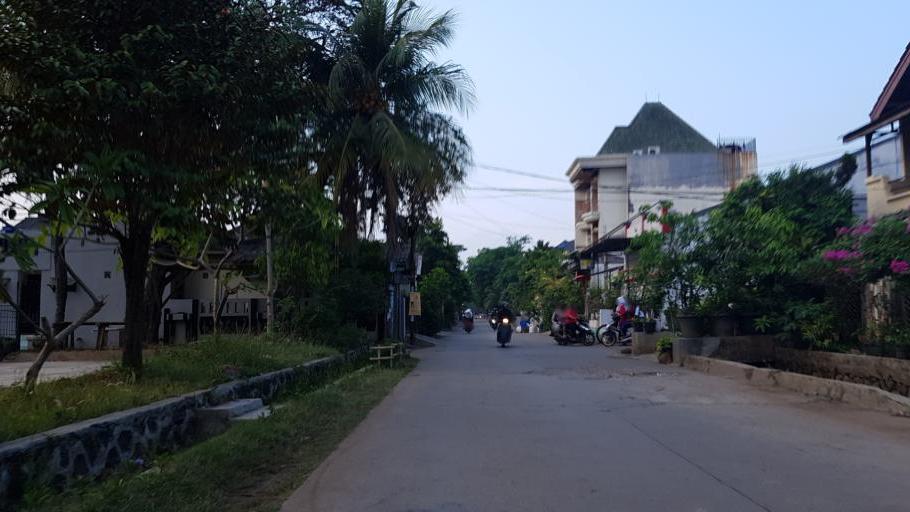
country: ID
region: West Java
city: Bekasi
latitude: -6.2733
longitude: 106.9476
